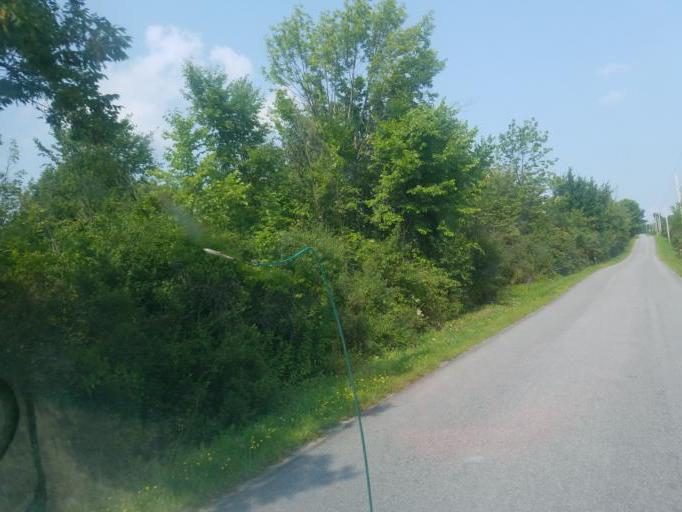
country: US
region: New York
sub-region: Montgomery County
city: Wellsville
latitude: 42.8612
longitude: -74.3310
